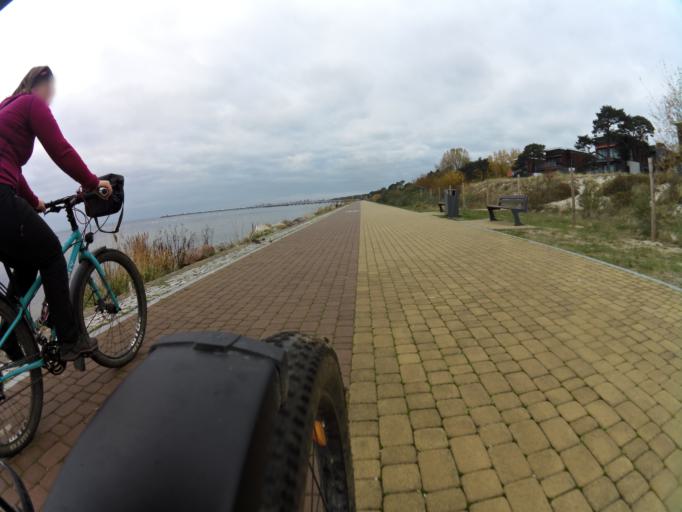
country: PL
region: Pomeranian Voivodeship
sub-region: Powiat pucki
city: Jastarnia
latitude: 54.6788
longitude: 18.7151
